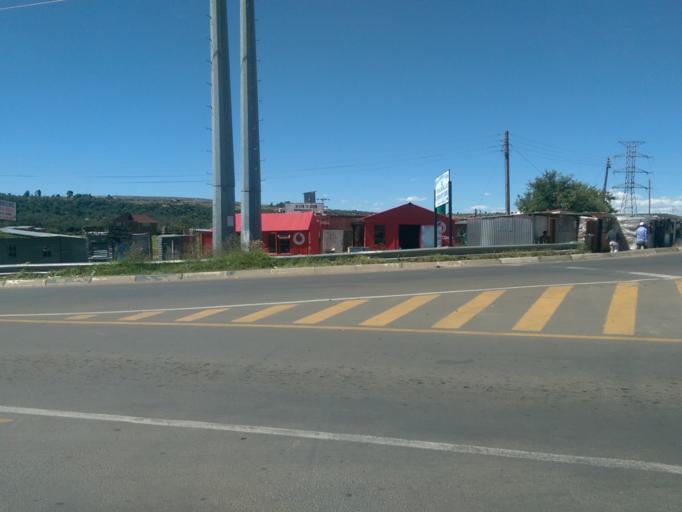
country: LS
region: Maseru
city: Maseru
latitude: -29.4044
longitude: 27.5615
